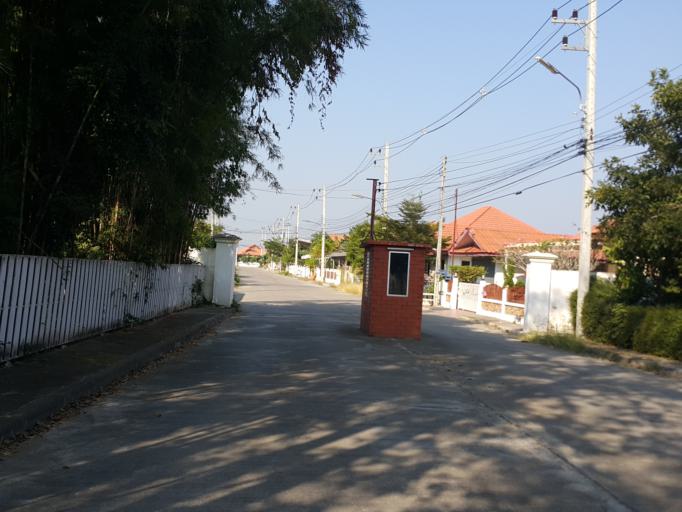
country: TH
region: Chiang Mai
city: San Kamphaeng
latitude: 18.7786
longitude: 99.0818
